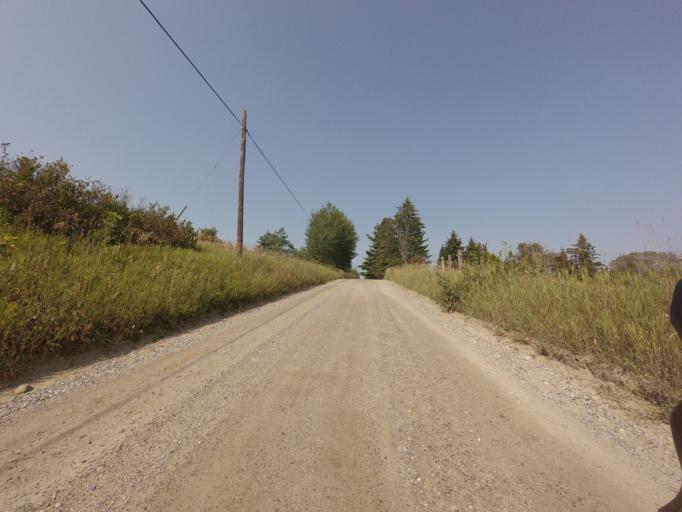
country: CA
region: Ontario
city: Skatepark
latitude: 44.7685
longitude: -76.8133
